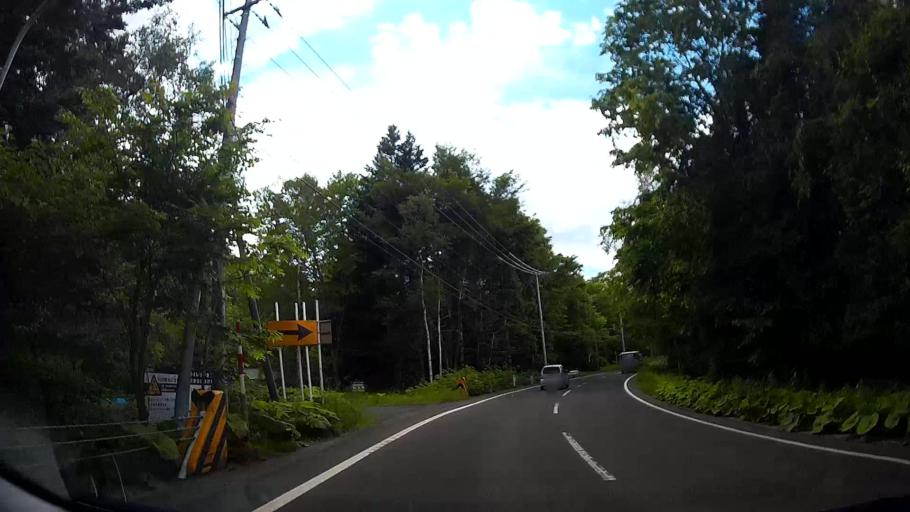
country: JP
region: Hokkaido
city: Kitahiroshima
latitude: 42.8423
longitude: 141.4781
